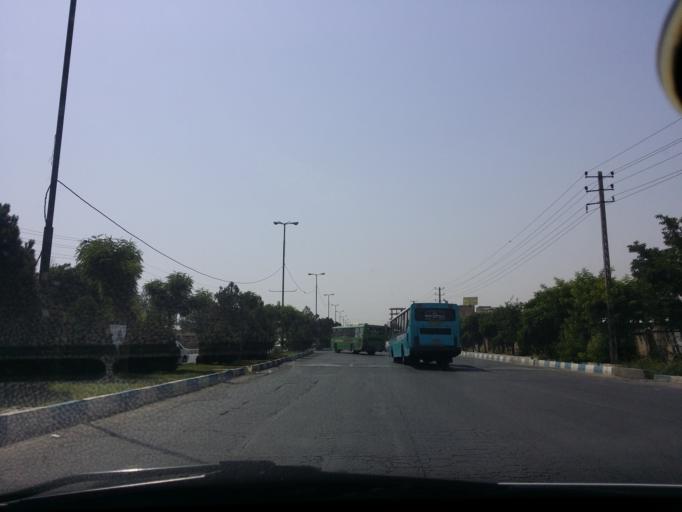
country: IR
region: Alborz
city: Karaj
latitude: 35.8551
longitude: 50.8968
